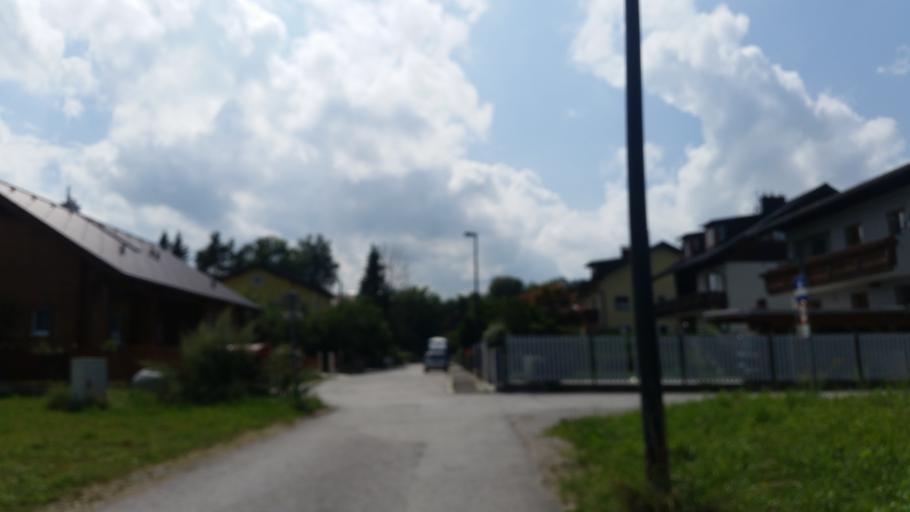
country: AT
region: Salzburg
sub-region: Politischer Bezirk Salzburg-Umgebung
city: Bergheim
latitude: 47.8280
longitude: 13.0134
